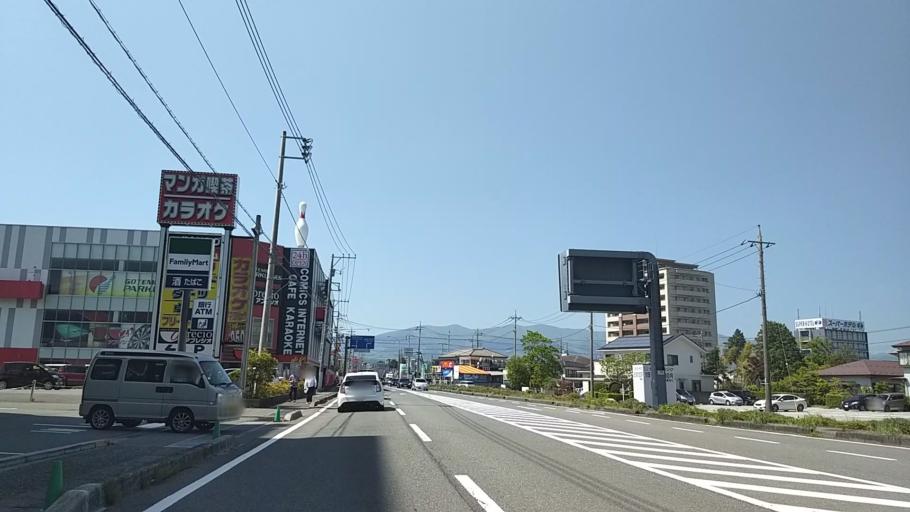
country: JP
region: Shizuoka
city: Gotemba
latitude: 35.2950
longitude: 138.9446
